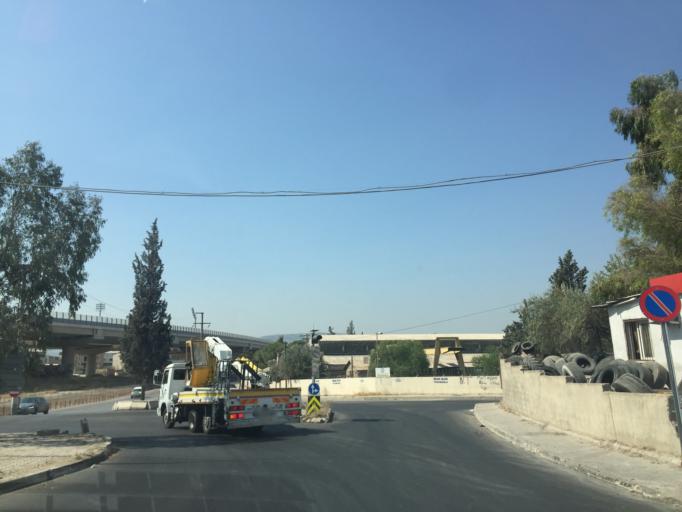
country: TR
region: Izmir
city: Bornova
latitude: 38.4516
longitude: 27.2649
